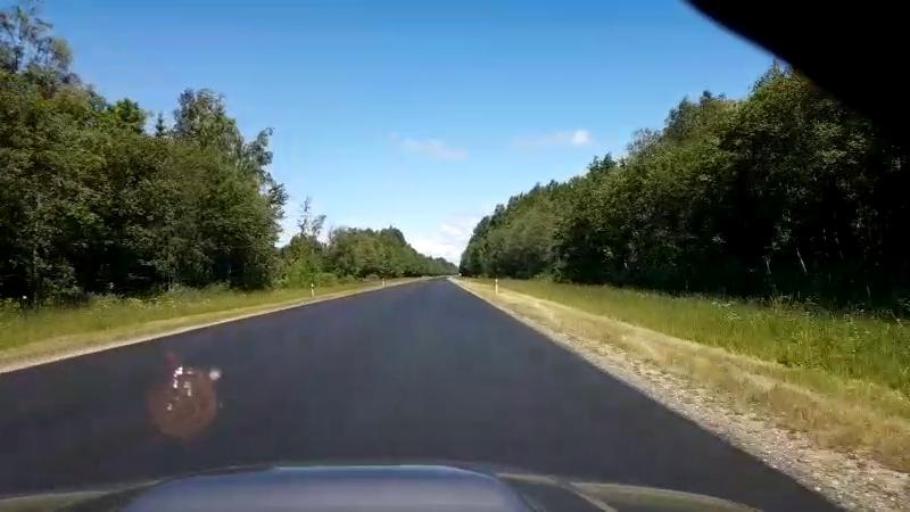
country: LV
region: Salacgrivas
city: Ainazi
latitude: 57.9437
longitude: 24.4329
